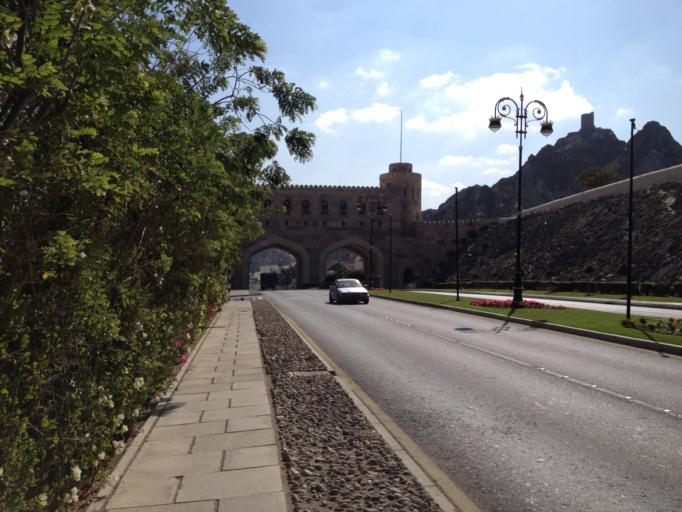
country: OM
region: Muhafazat Masqat
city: Muscat
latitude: 23.6186
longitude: 58.5864
